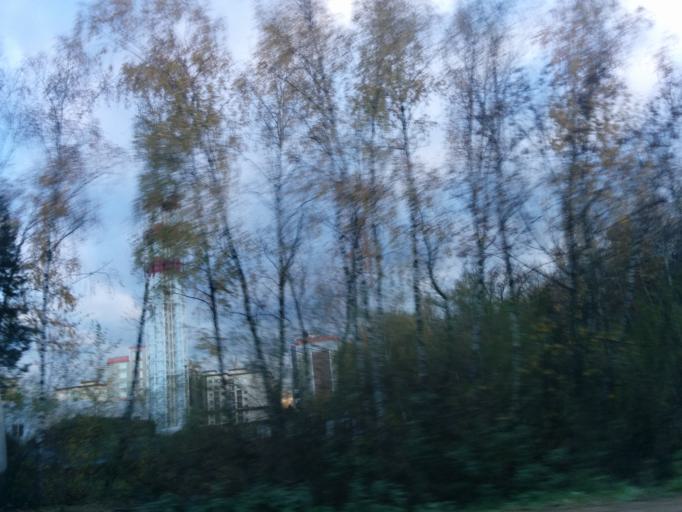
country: RU
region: Moscow
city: Zagor'ye
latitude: 55.5386
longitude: 37.6354
